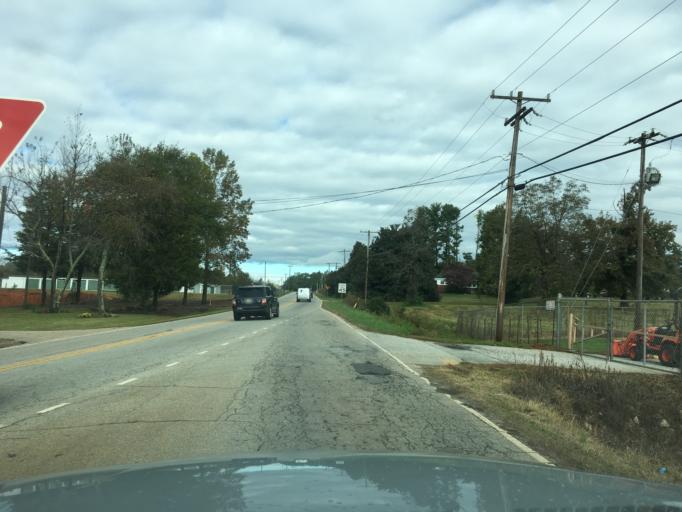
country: US
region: South Carolina
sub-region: Greenville County
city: Greer
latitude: 34.9928
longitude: -82.2456
